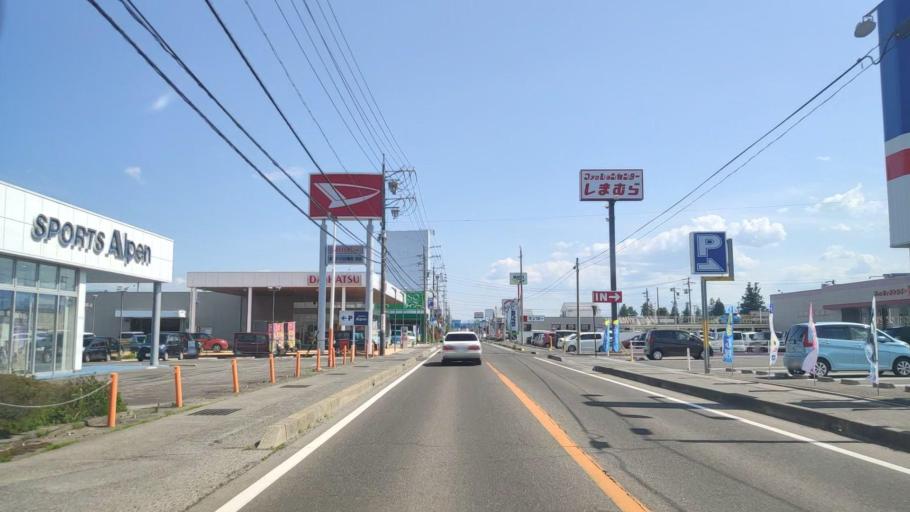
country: JP
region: Nagano
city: Hotaka
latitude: 36.3282
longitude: 137.8923
